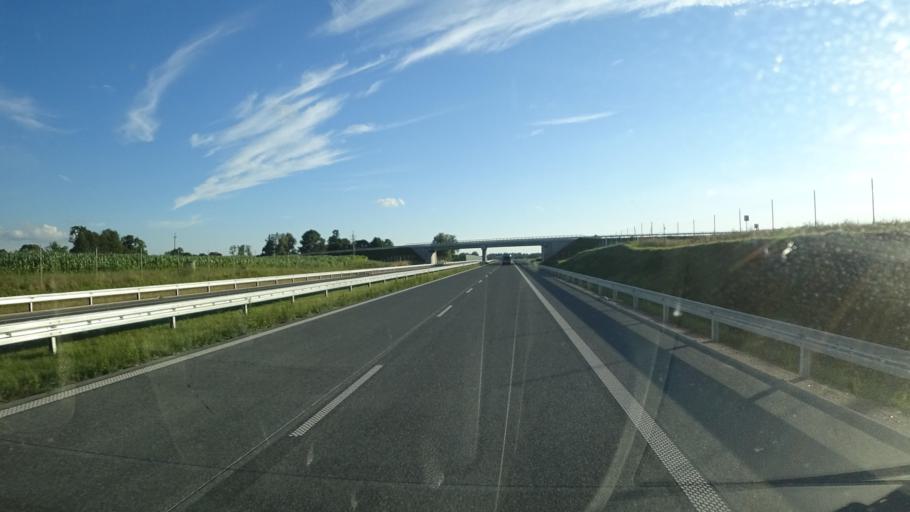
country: PL
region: Podlasie
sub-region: Powiat suwalski
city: Raczki
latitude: 53.9120
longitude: 22.7212
